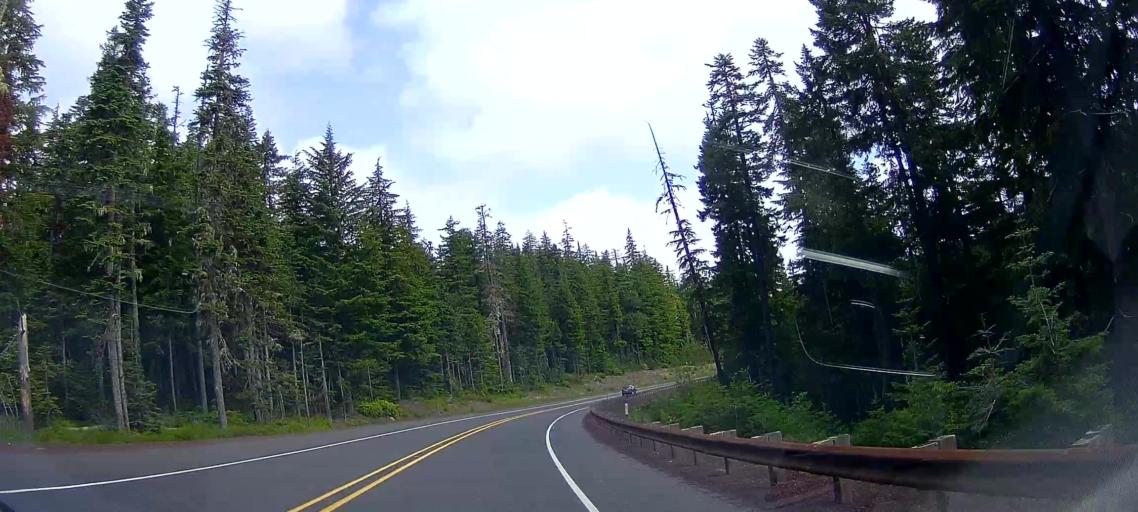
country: US
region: Oregon
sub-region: Clackamas County
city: Mount Hood Village
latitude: 45.2200
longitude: -121.6985
